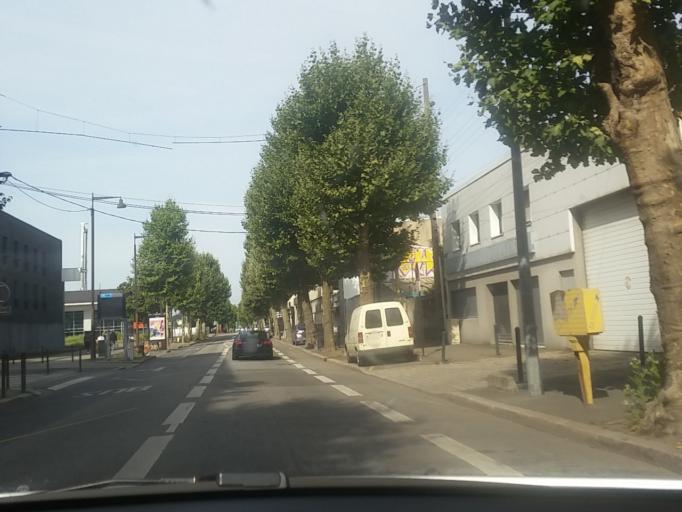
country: FR
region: Pays de la Loire
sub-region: Departement de la Loire-Atlantique
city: Nantes
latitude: 47.2050
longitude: -1.5581
